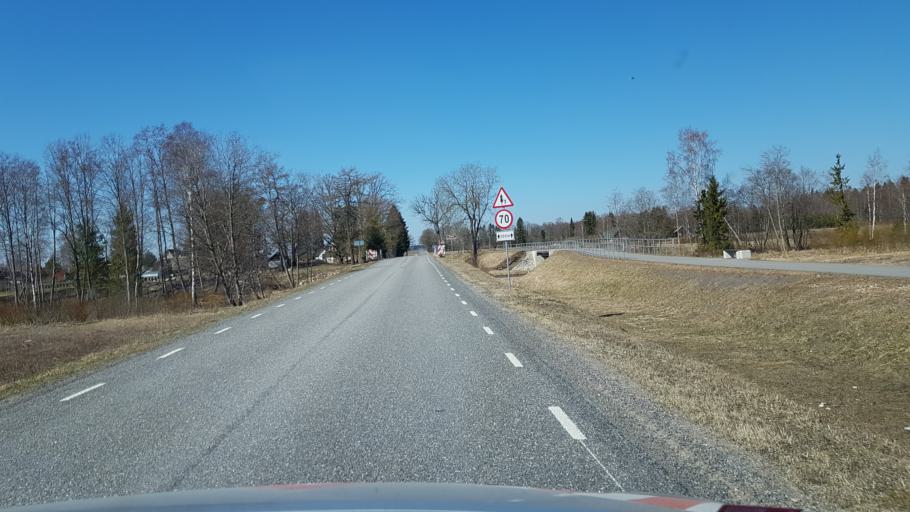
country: EE
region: Laeaene-Virumaa
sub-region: Rakke vald
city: Rakke
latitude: 58.9981
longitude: 26.2074
